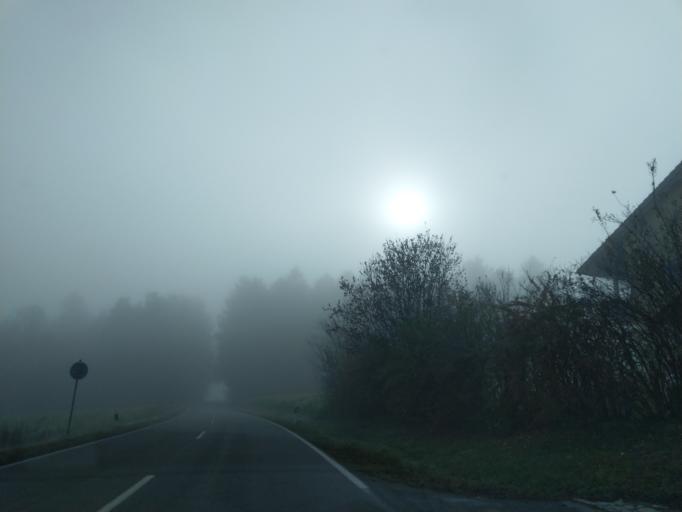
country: DE
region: Bavaria
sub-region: Lower Bavaria
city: Schollnach
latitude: 48.7468
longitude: 13.1868
